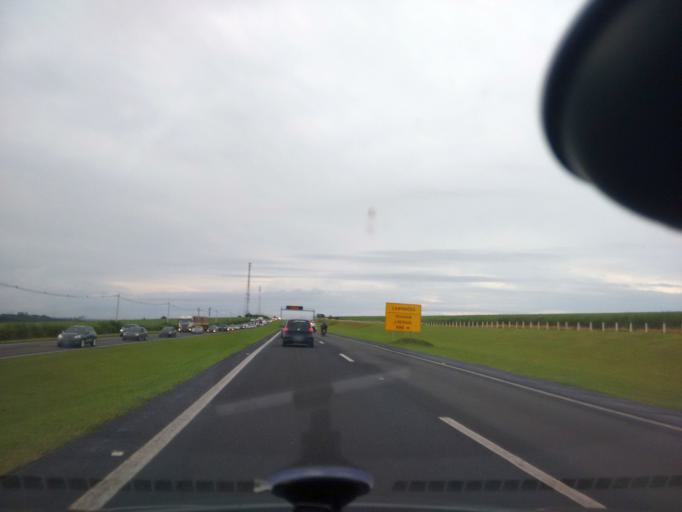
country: BR
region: Sao Paulo
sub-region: Itirapina
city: Itirapina
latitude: -22.1982
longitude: -47.7741
